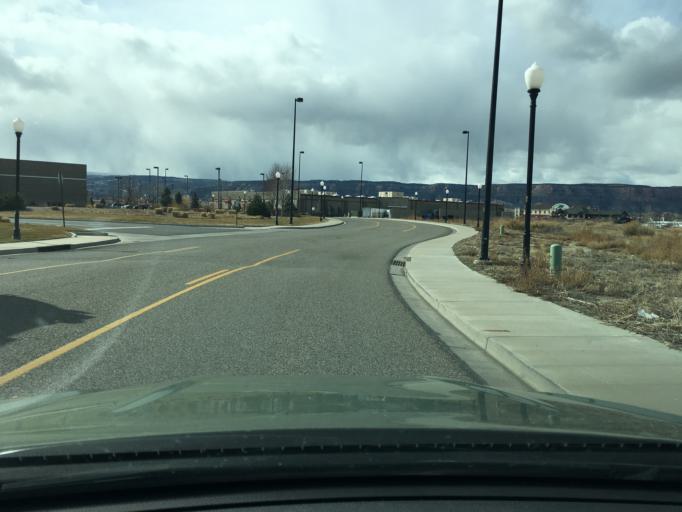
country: US
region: Colorado
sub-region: Mesa County
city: Redlands
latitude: 39.0982
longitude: -108.6056
